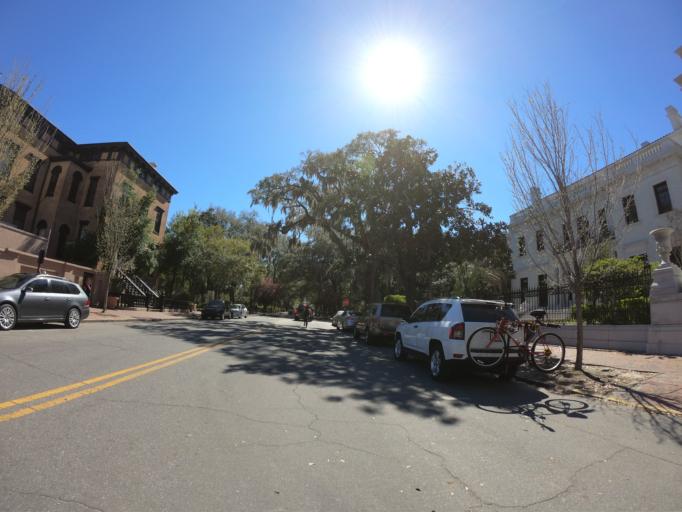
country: US
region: Georgia
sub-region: Chatham County
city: Savannah
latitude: 32.0706
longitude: -81.0951
